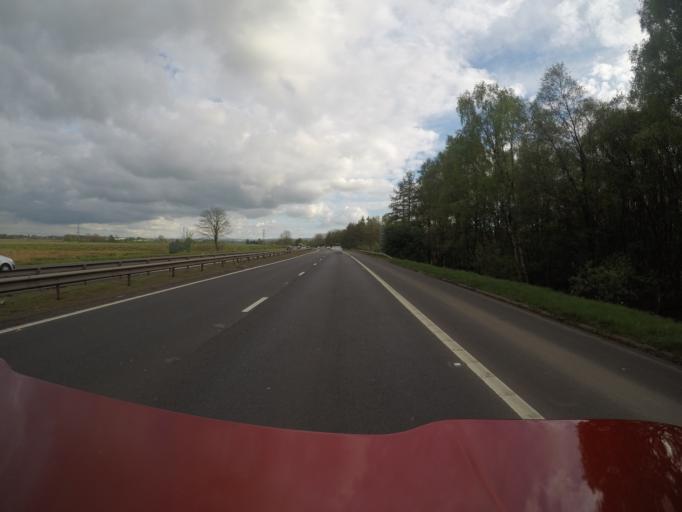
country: GB
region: Scotland
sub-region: Renfrewshire
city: Erskine
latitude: 55.8840
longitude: -4.4796
